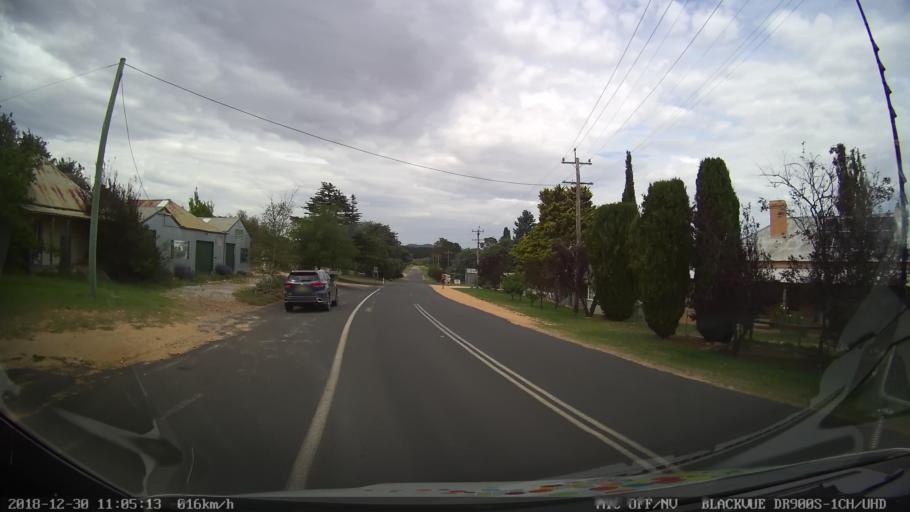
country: AU
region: New South Wales
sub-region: Snowy River
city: Berridale
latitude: -36.5025
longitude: 148.8352
